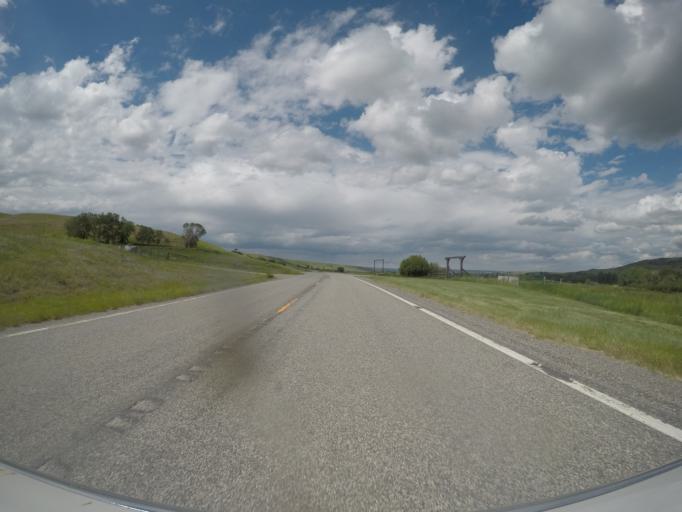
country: US
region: Montana
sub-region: Sweet Grass County
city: Big Timber
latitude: 45.7585
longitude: -109.9907
